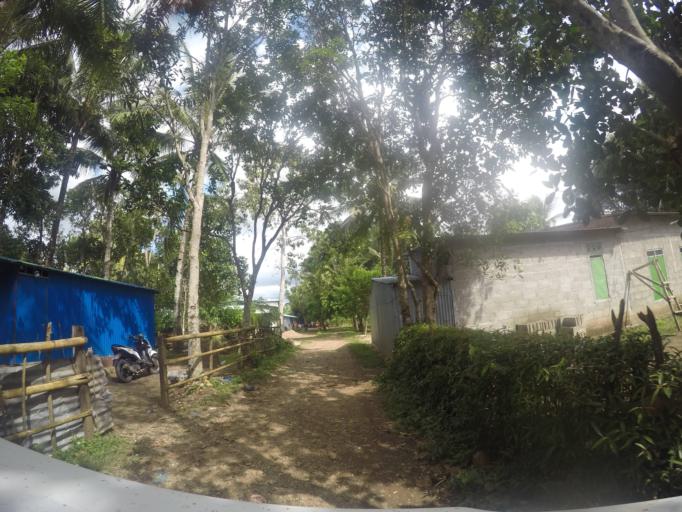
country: TL
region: Lautem
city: Lospalos
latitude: -8.5032
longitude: 127.0081
